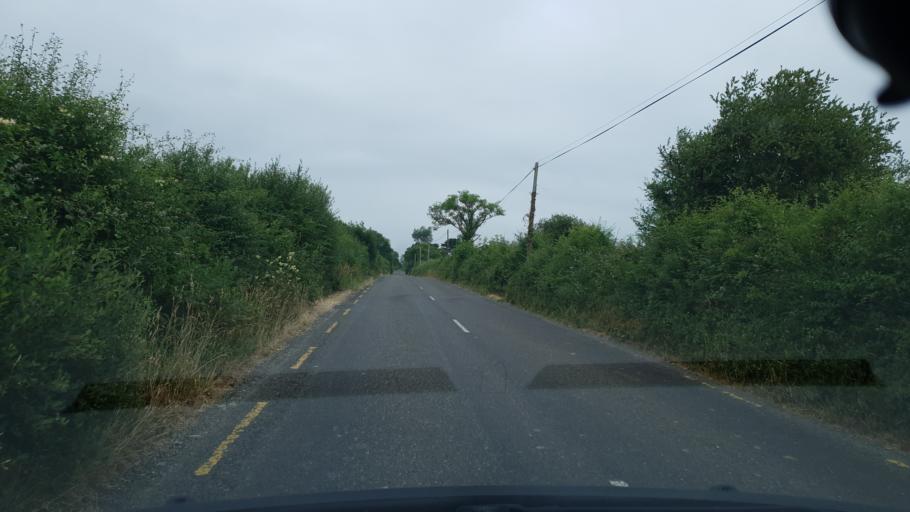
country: IE
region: Munster
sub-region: Ciarrai
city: Tralee
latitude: 52.1624
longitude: -9.6453
